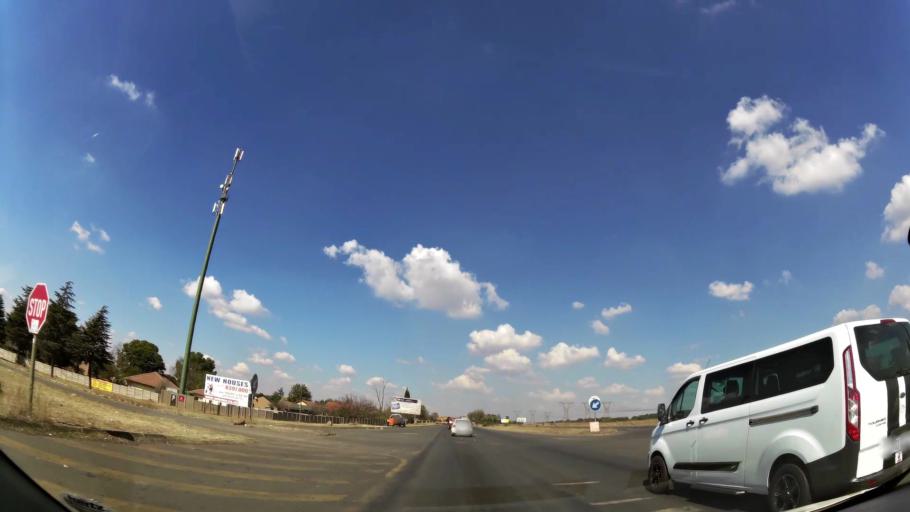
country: ZA
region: Mpumalanga
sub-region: Nkangala District Municipality
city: Witbank
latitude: -25.9399
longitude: 29.2414
